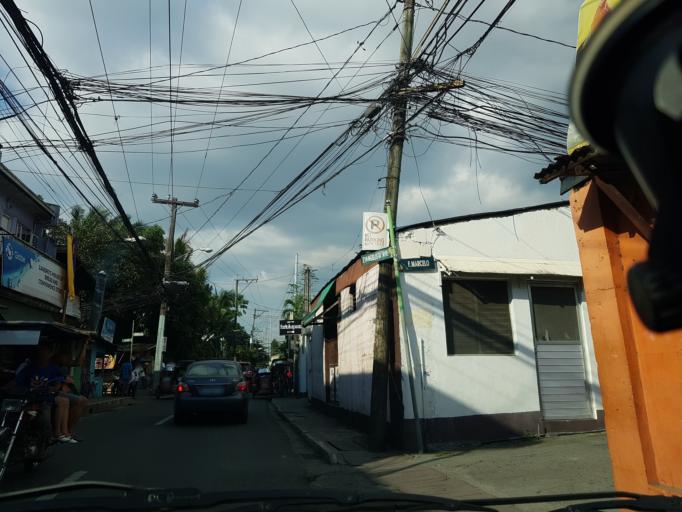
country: PH
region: Metro Manila
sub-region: Marikina
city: Calumpang
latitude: 14.6179
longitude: 121.0815
